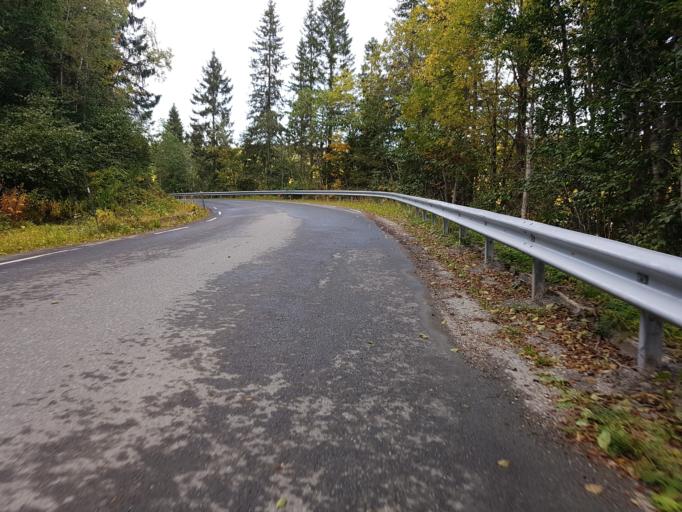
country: NO
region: Sor-Trondelag
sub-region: Klaebu
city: Klaebu
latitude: 63.3433
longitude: 10.5529
